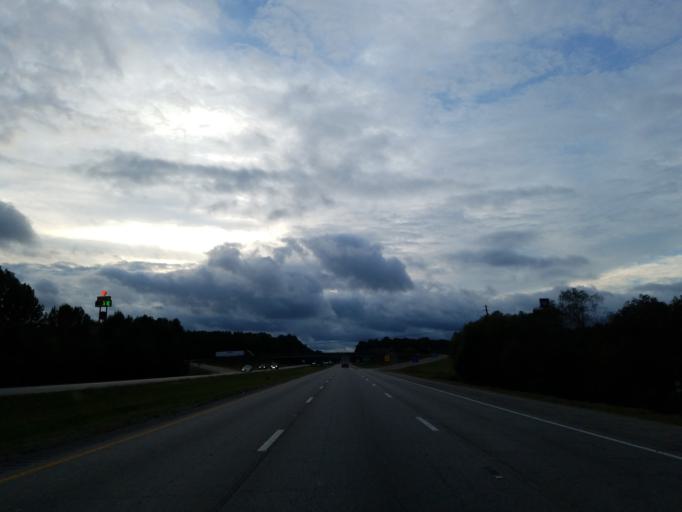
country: US
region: Mississippi
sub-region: Lauderdale County
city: Marion
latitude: 32.4137
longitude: -88.5026
